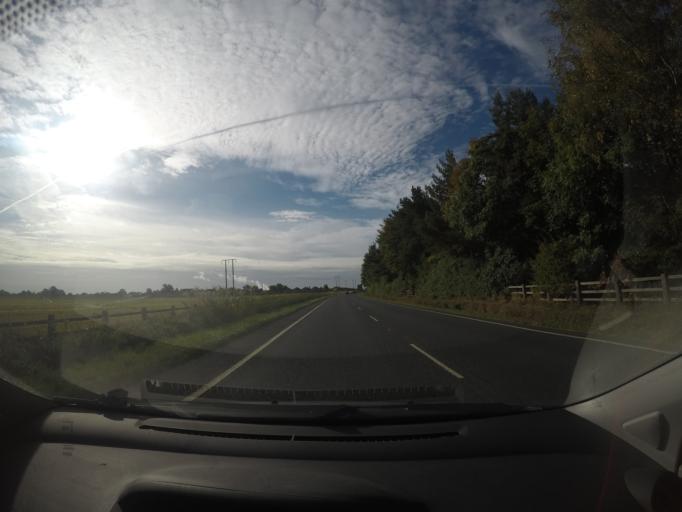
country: GB
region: England
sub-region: North Yorkshire
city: Barlby
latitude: 53.8011
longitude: -1.0358
